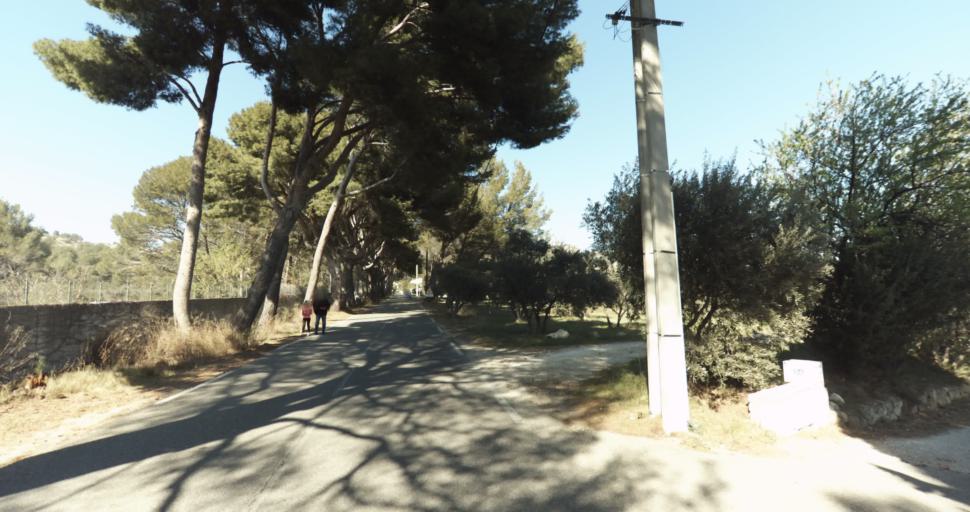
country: FR
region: Provence-Alpes-Cote d'Azur
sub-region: Departement des Bouches-du-Rhone
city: Pelissanne
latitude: 43.6448
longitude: 5.1549
